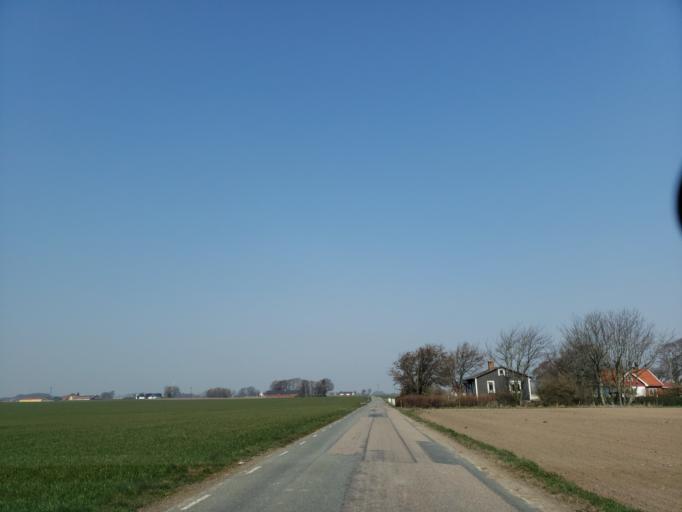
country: SE
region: Skane
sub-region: Simrishamns Kommun
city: Simrishamn
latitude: 55.4479
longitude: 14.2173
